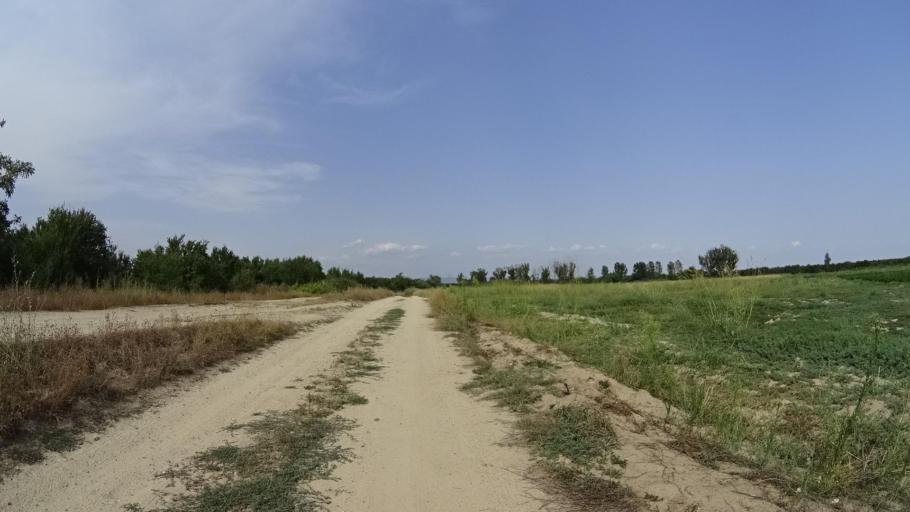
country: BG
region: Plovdiv
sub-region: Obshtina Kaloyanovo
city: Kaloyanovo
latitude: 42.2960
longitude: 24.7960
